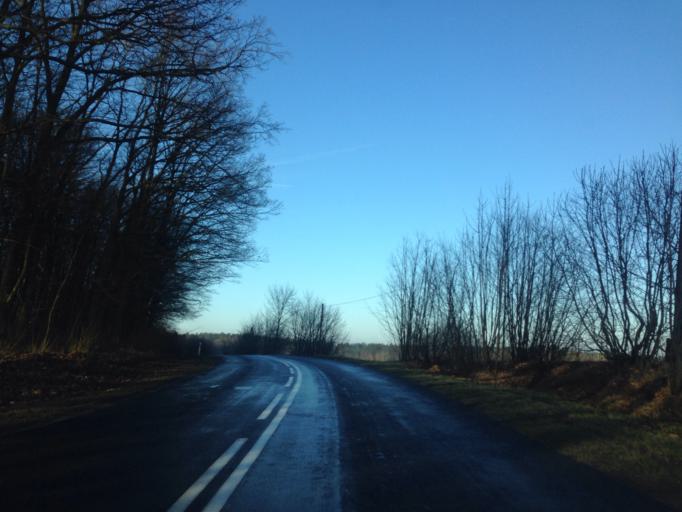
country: PL
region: Kujawsko-Pomorskie
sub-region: Powiat brodnicki
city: Bobrowo
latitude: 53.3213
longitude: 19.2688
